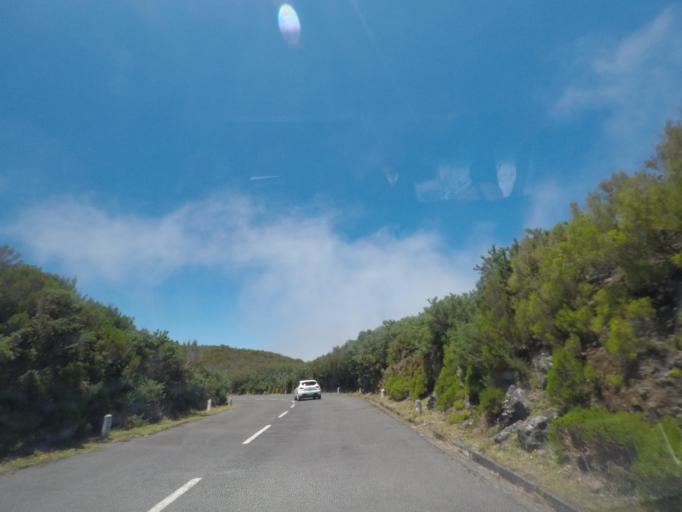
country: PT
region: Madeira
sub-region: Porto Moniz
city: Porto Moniz
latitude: 32.8067
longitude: -17.1925
